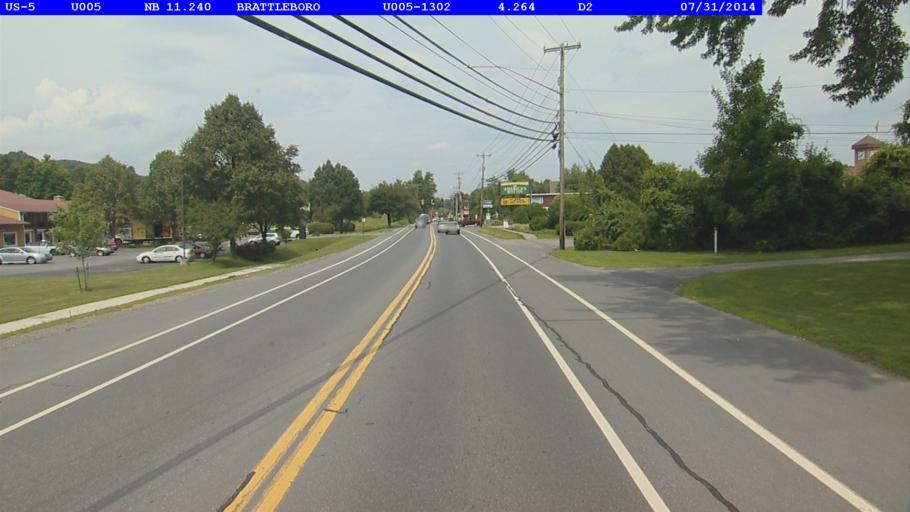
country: US
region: Vermont
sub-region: Windham County
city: Brattleboro
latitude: 42.8802
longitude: -72.5590
